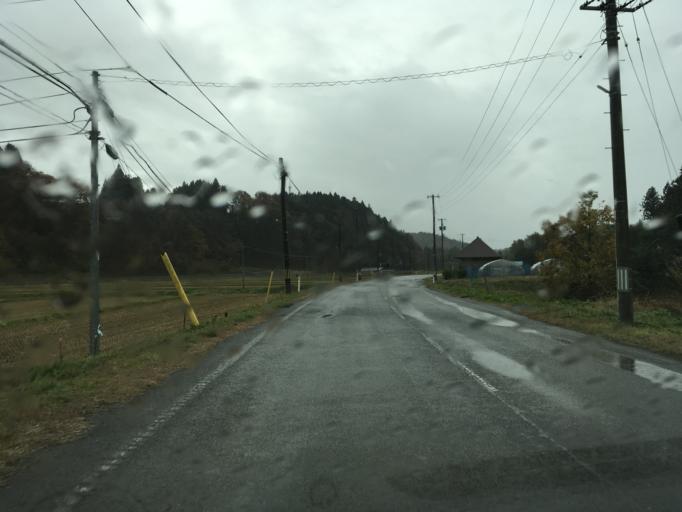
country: JP
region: Iwate
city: Ichinoseki
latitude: 38.8000
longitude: 141.2493
